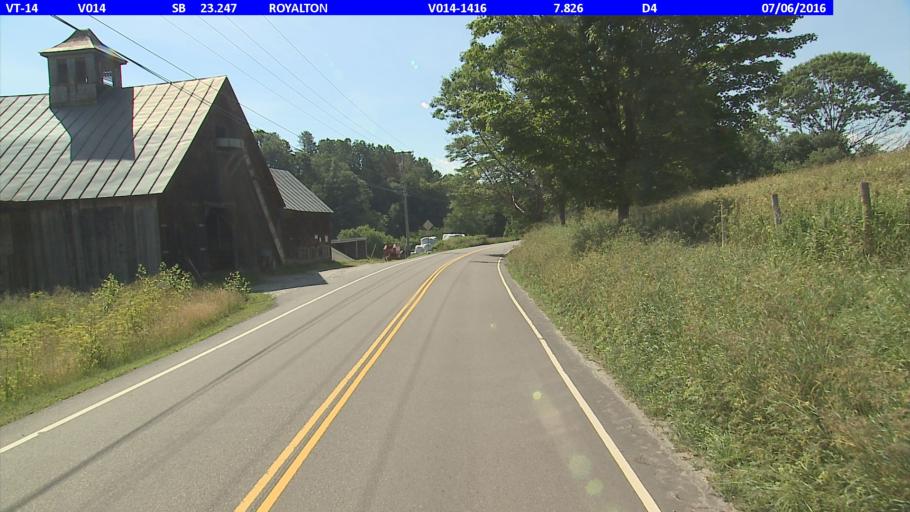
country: US
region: Vermont
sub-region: Orange County
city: Randolph
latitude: 43.8479
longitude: -72.5879
